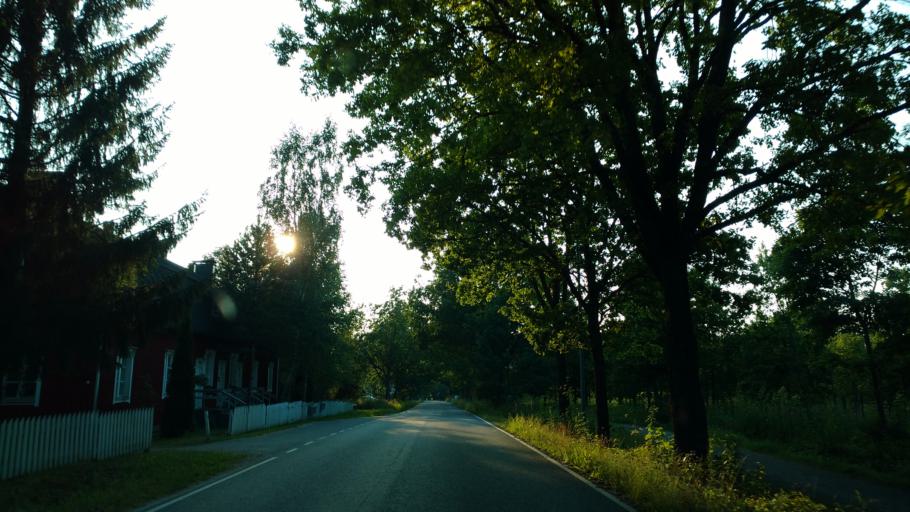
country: FI
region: Varsinais-Suomi
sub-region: Salo
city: Saerkisalo
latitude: 60.2159
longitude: 22.9126
